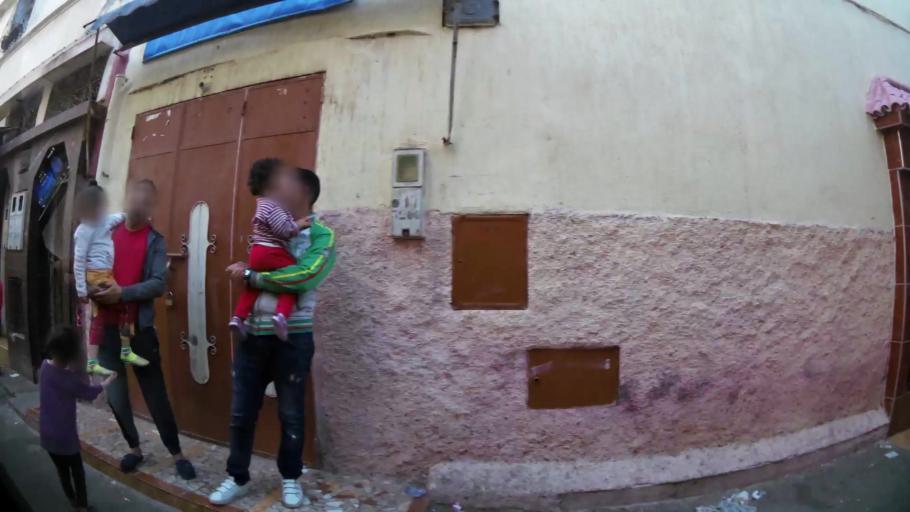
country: MA
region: Oued ed Dahab-Lagouira
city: Dakhla
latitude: 30.3877
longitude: -9.5686
